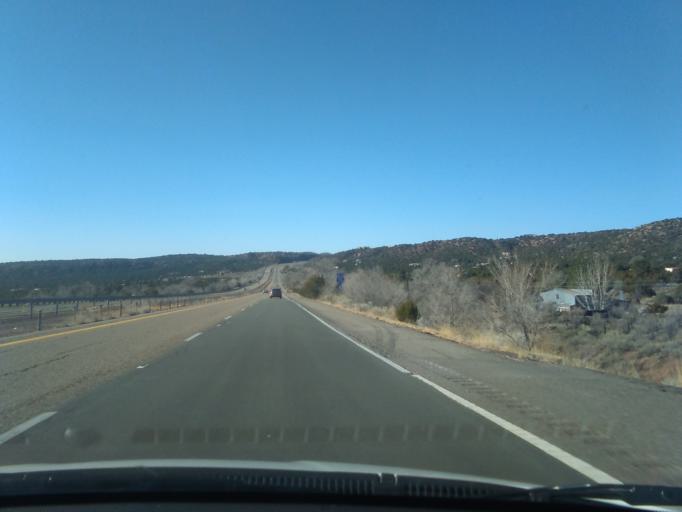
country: US
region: New Mexico
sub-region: Santa Fe County
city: Eldorado at Santa Fe
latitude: 35.5450
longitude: -105.8344
